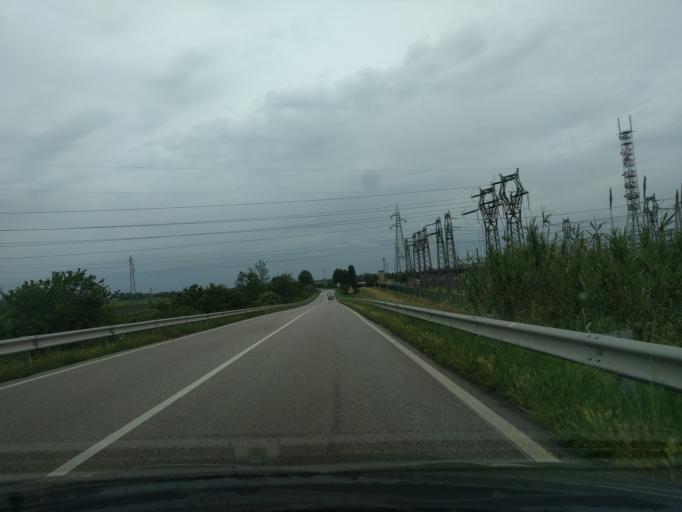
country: IT
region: Veneto
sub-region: Provincia di Rovigo
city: Loreo
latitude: 45.0513
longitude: 12.1411
